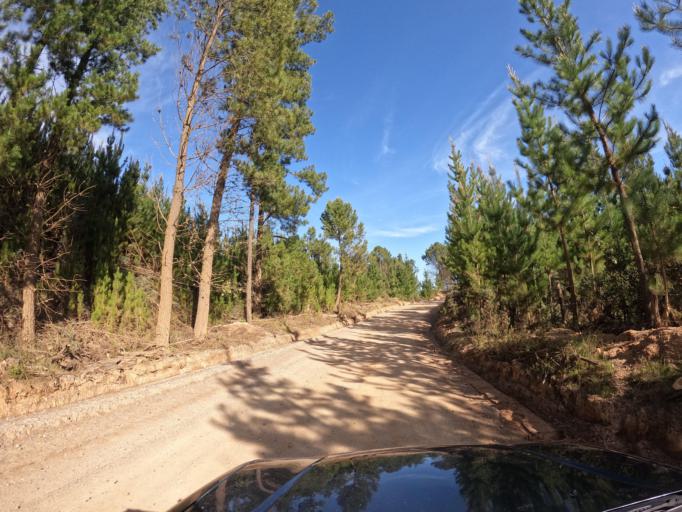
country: CL
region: Biobio
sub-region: Provincia de Biobio
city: La Laja
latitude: -37.1099
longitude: -72.7407
